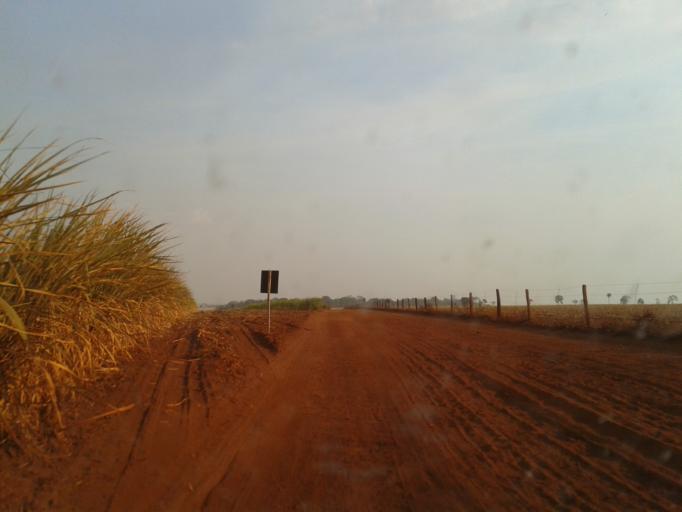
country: BR
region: Minas Gerais
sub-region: Capinopolis
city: Capinopolis
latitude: -18.7080
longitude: -49.6858
